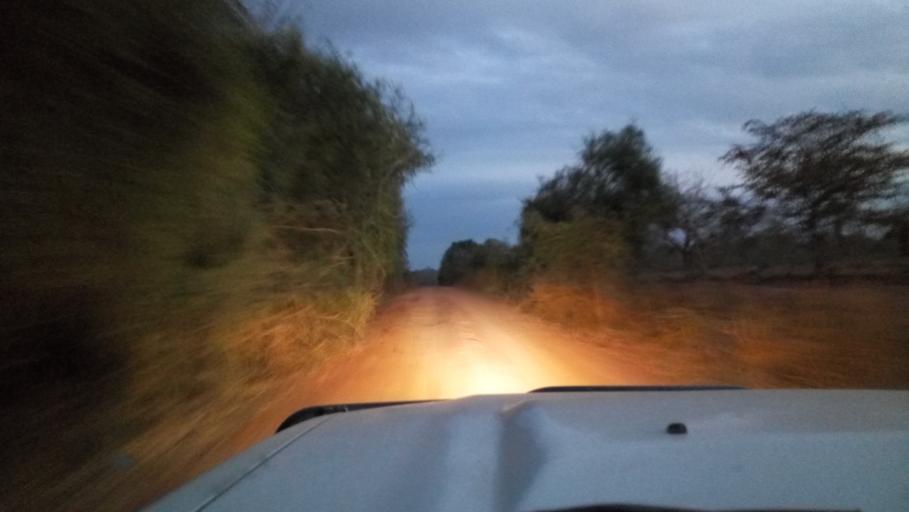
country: KE
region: Kitui
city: Kitui
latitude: -1.8004
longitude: 38.1896
